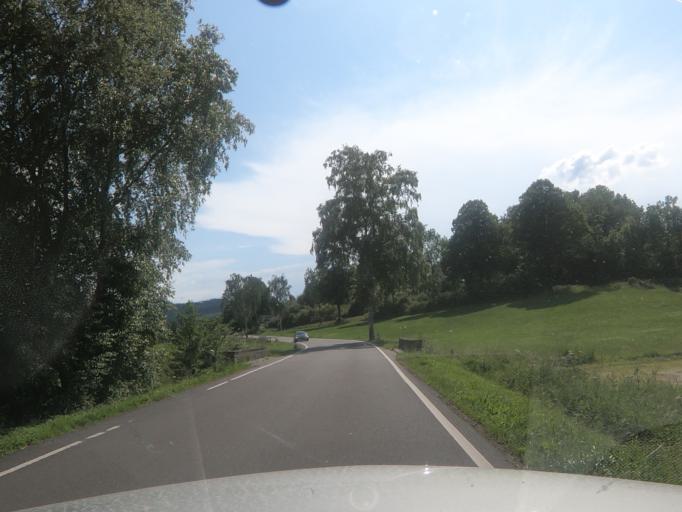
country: DE
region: North Rhine-Westphalia
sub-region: Regierungsbezirk Arnsberg
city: Finnentrop
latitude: 51.1110
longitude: 7.9606
